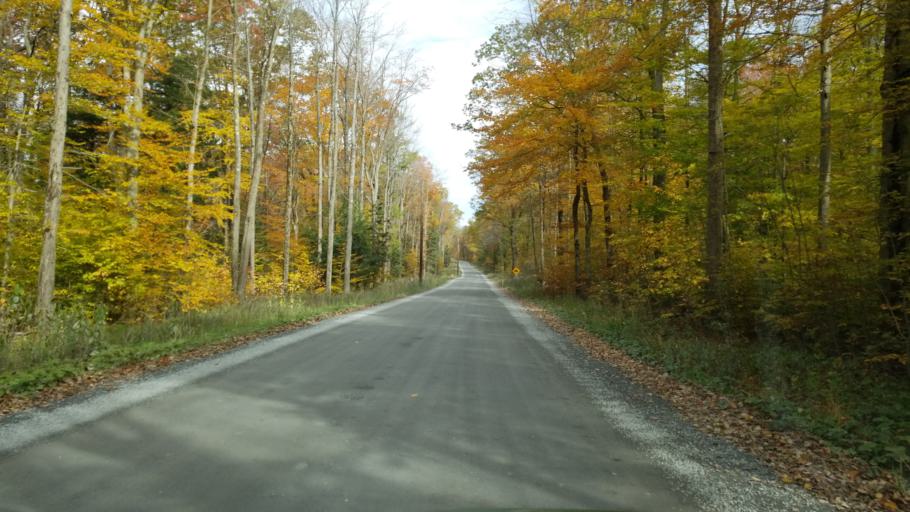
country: US
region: Pennsylvania
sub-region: Clearfield County
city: Clearfield
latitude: 41.1267
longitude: -78.5288
